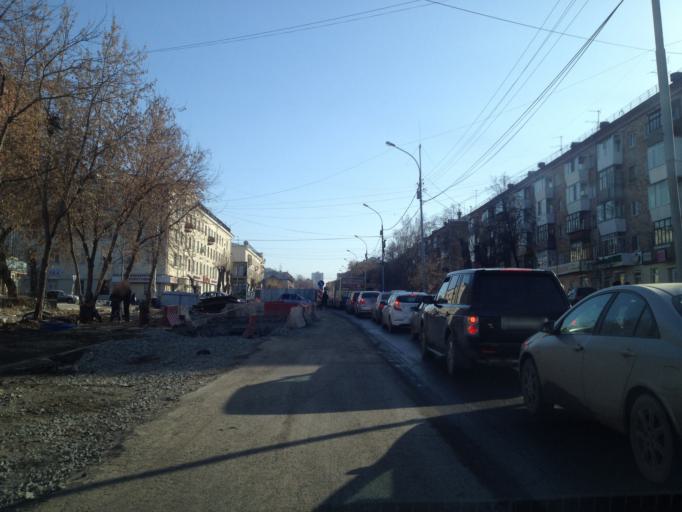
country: RU
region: Sverdlovsk
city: Yekaterinburg
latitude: 56.8383
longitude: 60.5536
